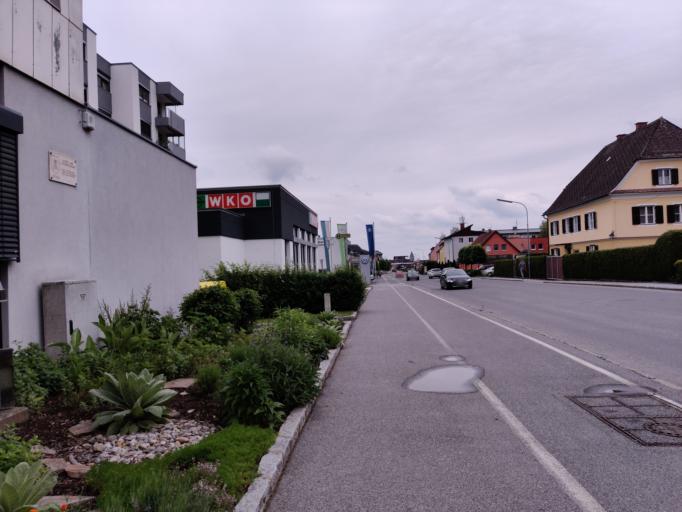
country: AT
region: Styria
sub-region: Politischer Bezirk Deutschlandsberg
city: Deutschlandsberg
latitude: 46.8179
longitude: 15.2225
